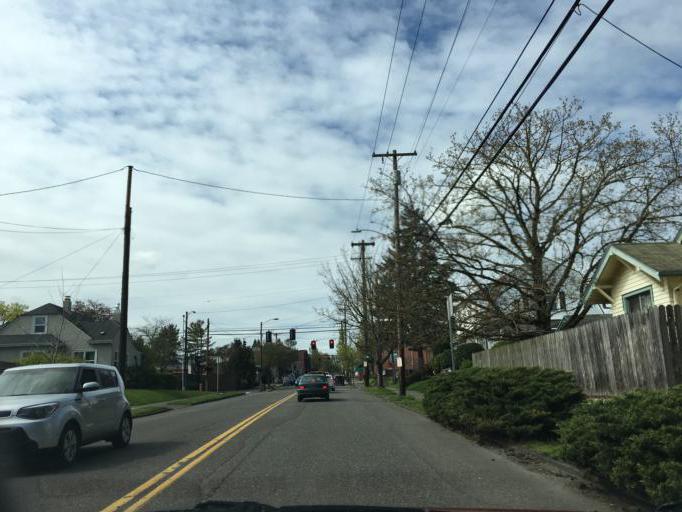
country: US
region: Oregon
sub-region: Clackamas County
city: Milwaukie
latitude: 45.4739
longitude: -122.6468
